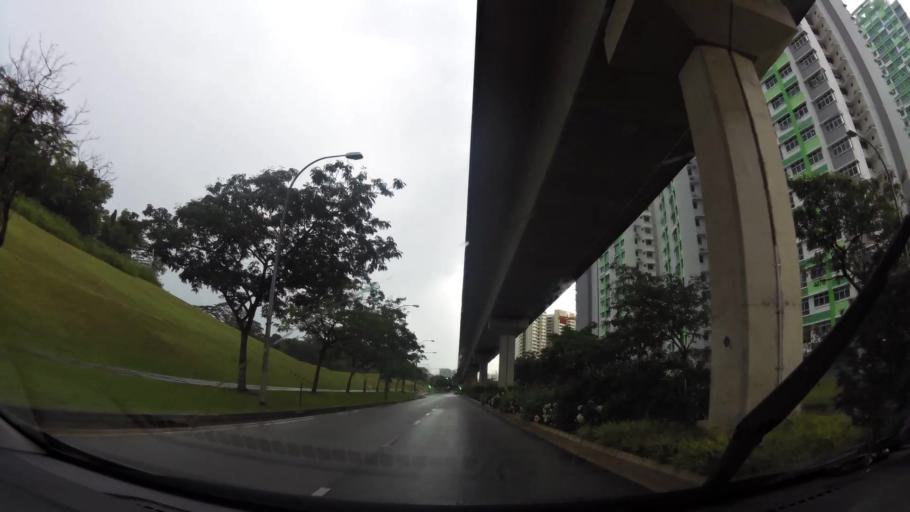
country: MY
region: Johor
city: Kampung Pasir Gudang Baru
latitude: 1.3986
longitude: 103.8777
